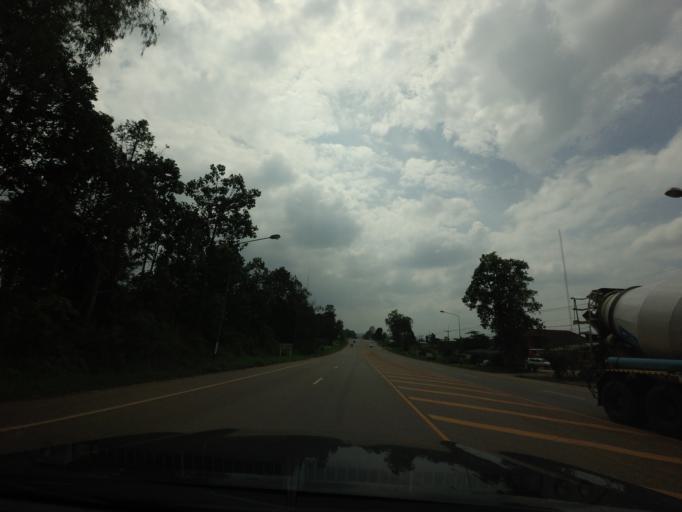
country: TH
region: Loei
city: Dan Sai
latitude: 17.3636
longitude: 101.2544
